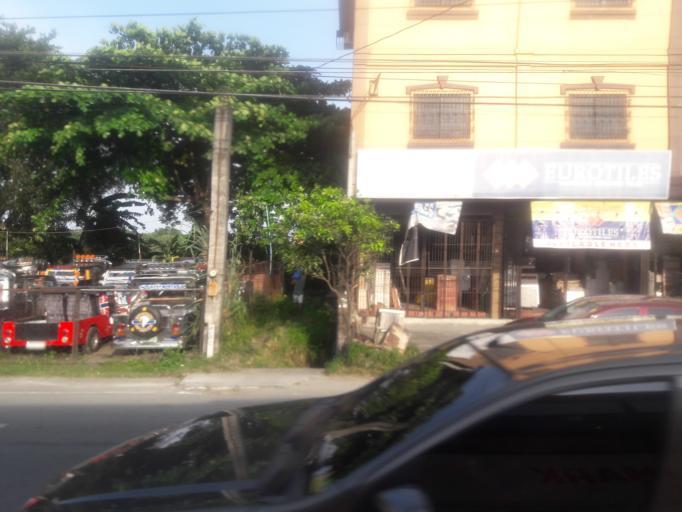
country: PH
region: Calabarzon
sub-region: Province of Cavite
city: Imus
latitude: 14.4098
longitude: 120.9406
